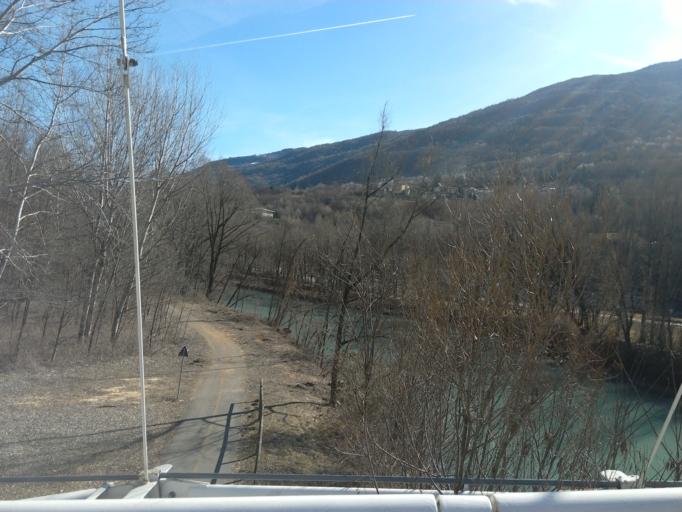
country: IT
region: Lombardy
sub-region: Provincia di Sondrio
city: Torchione-Moia
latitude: 46.1585
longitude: 9.8606
